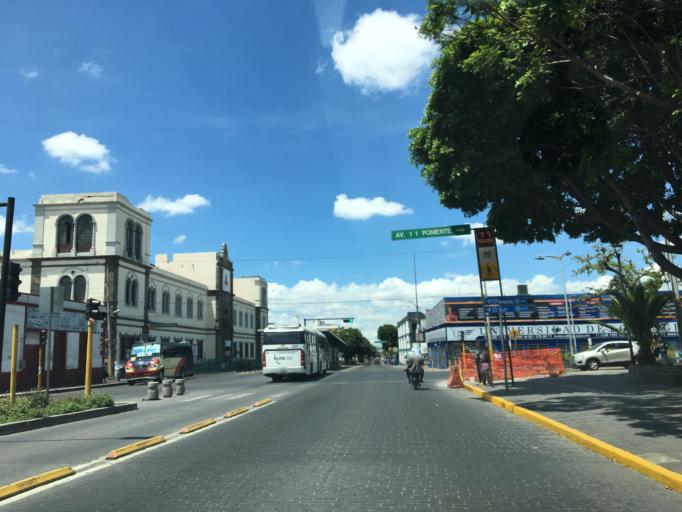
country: MX
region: Puebla
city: Puebla
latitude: 19.0450
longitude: -98.2084
